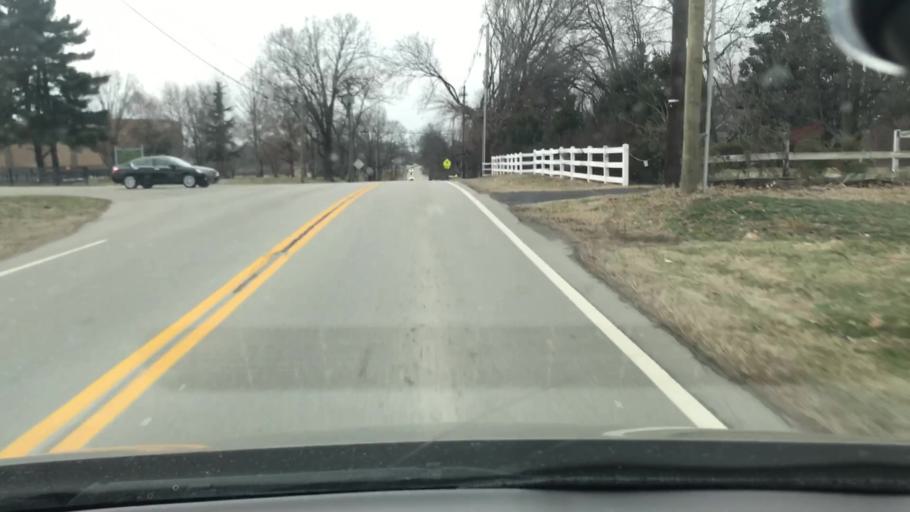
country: US
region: Kentucky
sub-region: Jefferson County
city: Graymoor-Devondale
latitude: 38.2865
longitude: -85.6234
